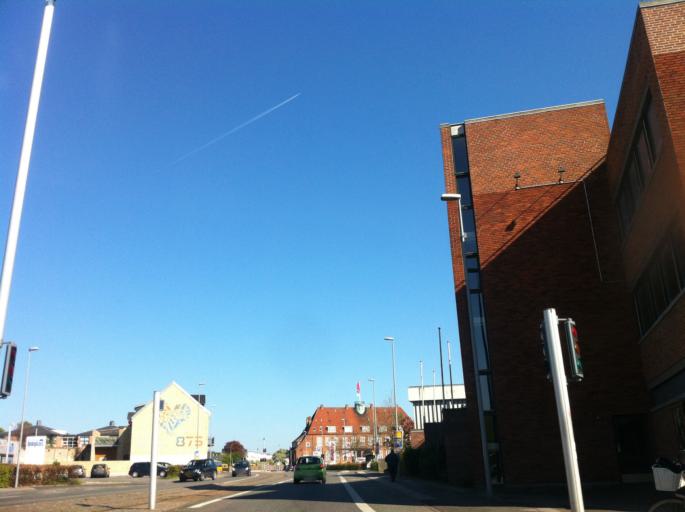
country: DK
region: Zealand
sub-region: Naestved Kommune
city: Naestved
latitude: 55.2342
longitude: 11.7602
